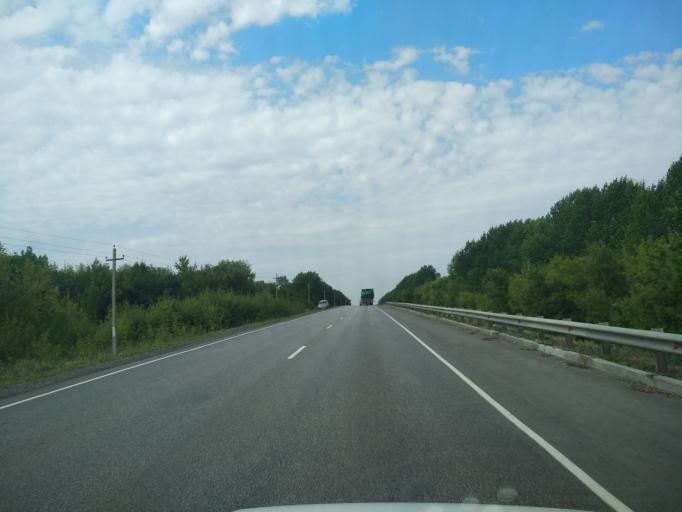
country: RU
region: Lipetsk
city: Dobrinka
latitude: 51.8925
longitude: 40.4443
